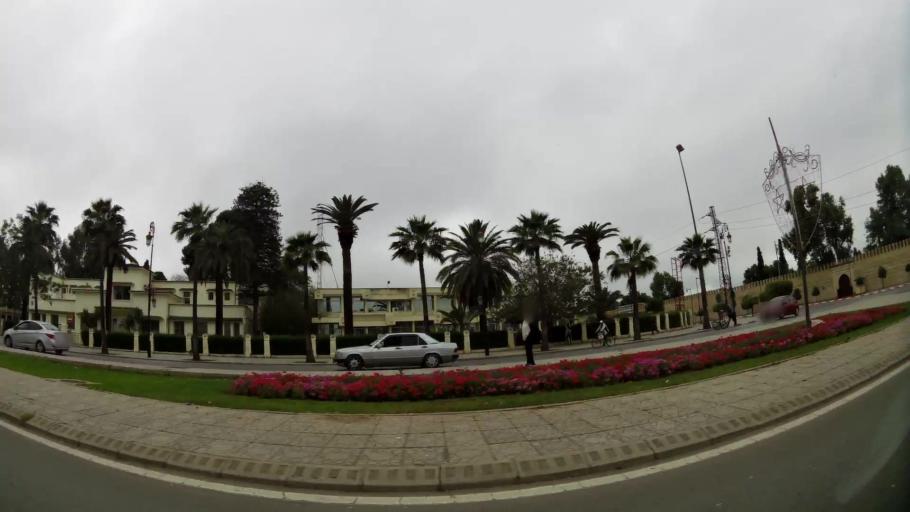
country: MA
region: Fes-Boulemane
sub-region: Fes
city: Fes
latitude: 34.0491
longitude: -4.9958
